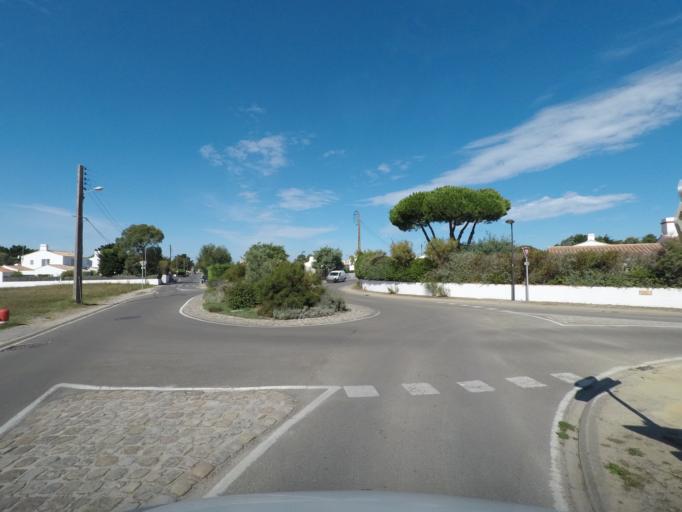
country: FR
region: Pays de la Loire
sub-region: Departement de la Vendee
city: La Gueriniere
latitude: 47.0027
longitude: -2.2291
